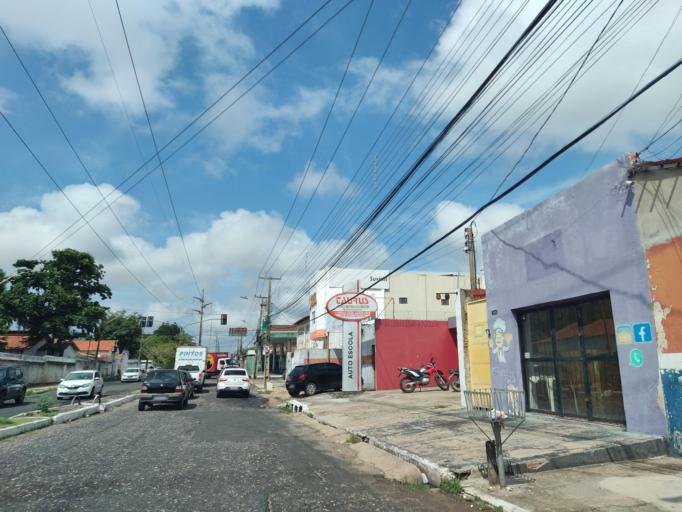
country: BR
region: Piaui
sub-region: Teresina
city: Teresina
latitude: -5.0733
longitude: -42.8100
